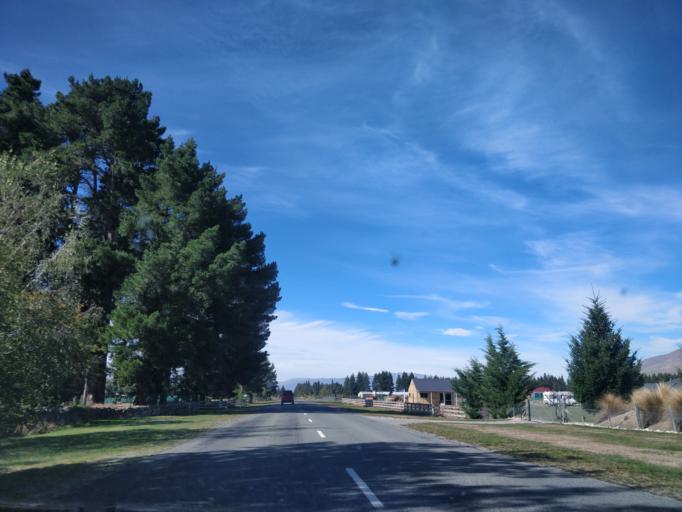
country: NZ
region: Otago
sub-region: Queenstown-Lakes District
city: Wanaka
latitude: -44.2403
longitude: 170.0831
